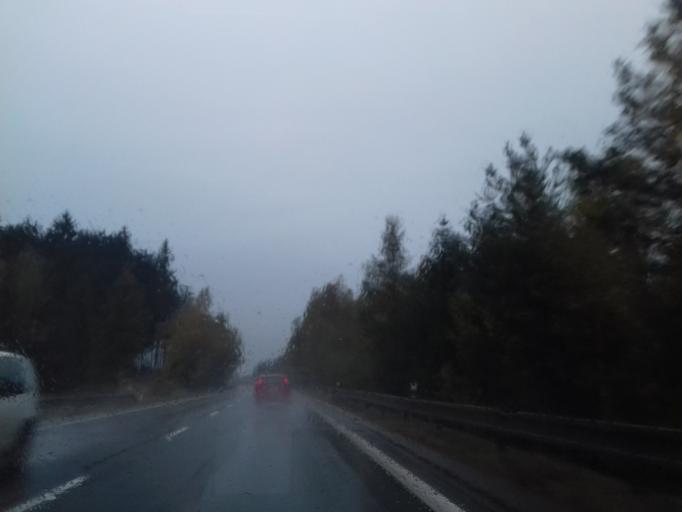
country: CZ
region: Pardubicky
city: Kuncina
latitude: 49.7530
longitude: 16.5620
